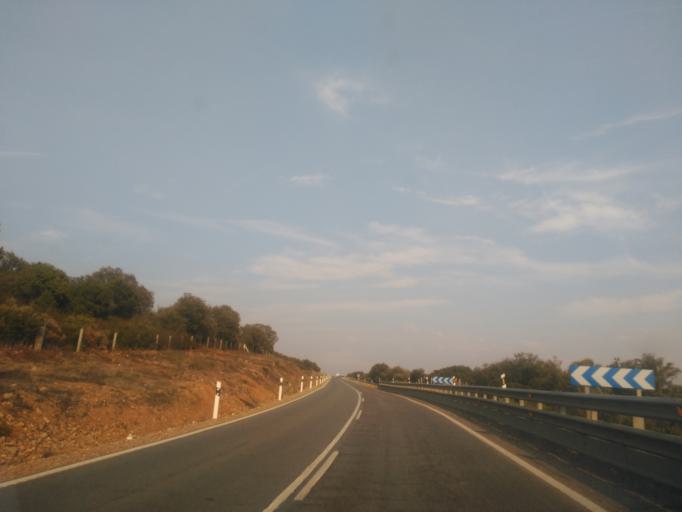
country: ES
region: Castille and Leon
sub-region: Provincia de Zamora
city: Perilla de Castro
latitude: 41.7489
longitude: -5.8534
